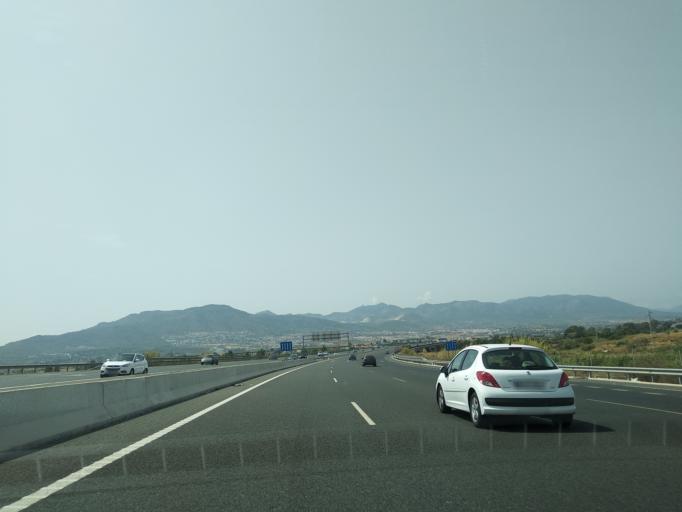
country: ES
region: Andalusia
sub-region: Provincia de Malaga
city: Alhaurin de la Torre
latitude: 36.7006
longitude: -4.5160
